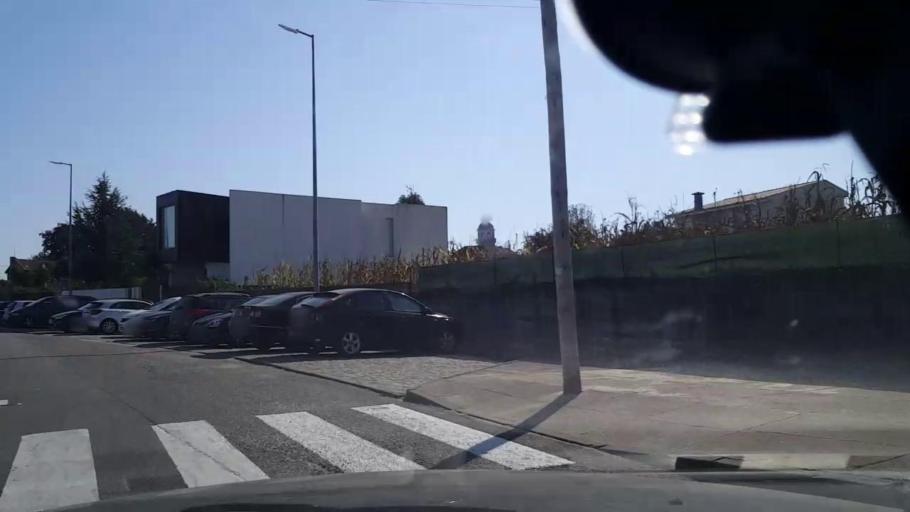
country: PT
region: Porto
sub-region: Vila do Conde
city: Arvore
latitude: 41.3799
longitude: -8.6827
